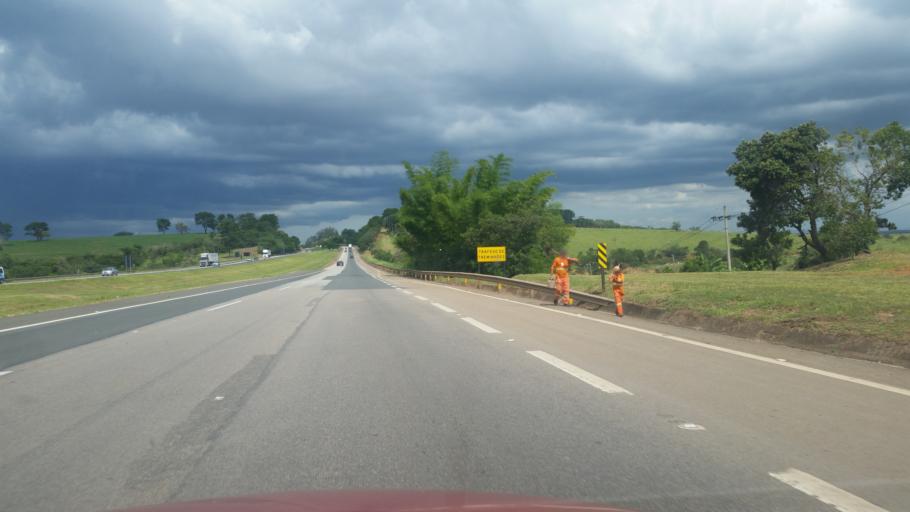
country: BR
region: Sao Paulo
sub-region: Boituva
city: Boituva
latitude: -23.2948
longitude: -47.7199
